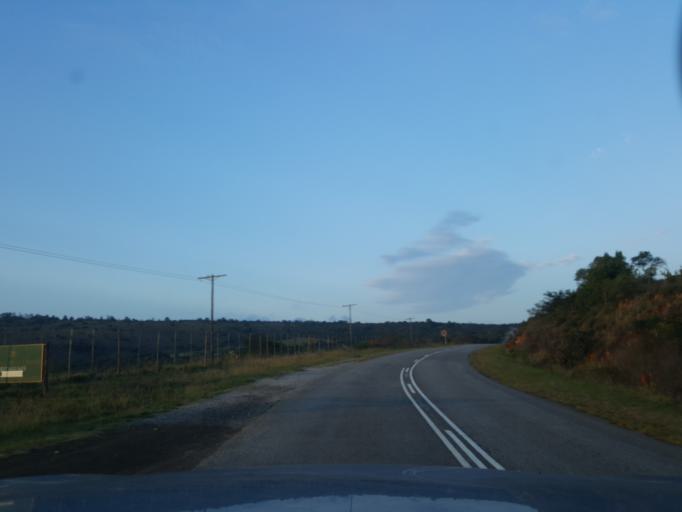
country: ZA
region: Eastern Cape
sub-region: Cacadu District Municipality
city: Grahamstown
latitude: -33.4626
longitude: 26.4837
